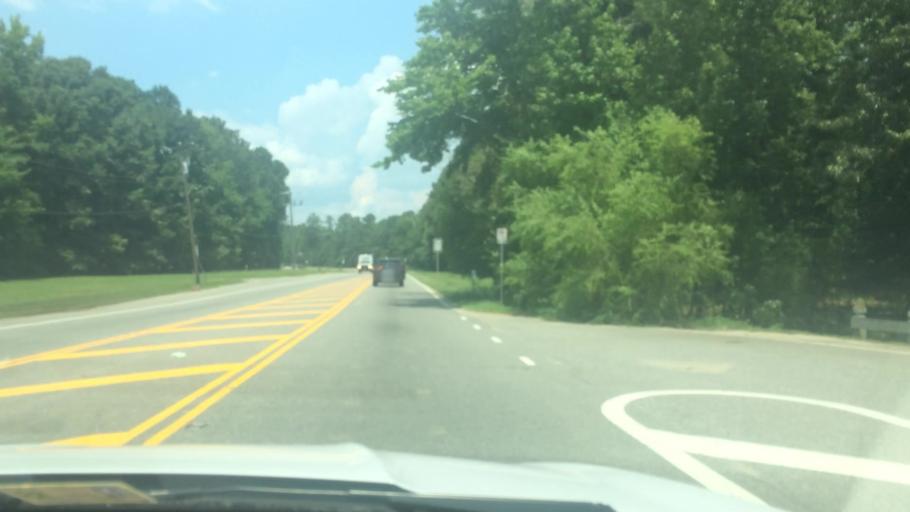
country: US
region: Virginia
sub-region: York County
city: Yorktown
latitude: 37.1777
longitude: -76.5698
